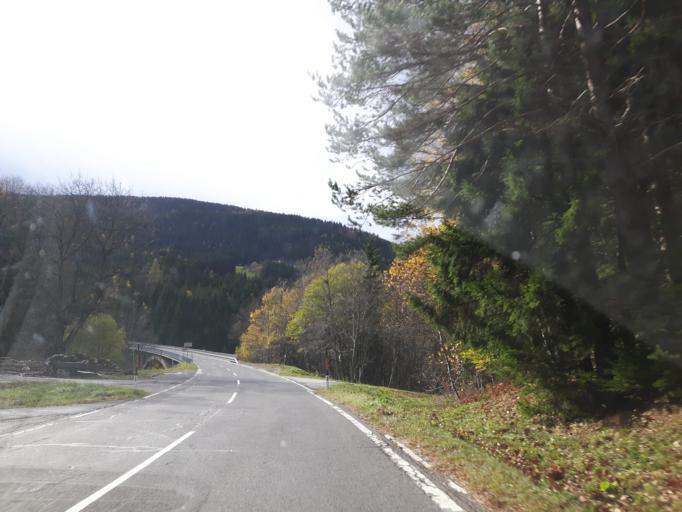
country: AT
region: Styria
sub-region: Politischer Bezirk Deutschlandsberg
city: Soboth
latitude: 46.7031
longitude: 15.0949
